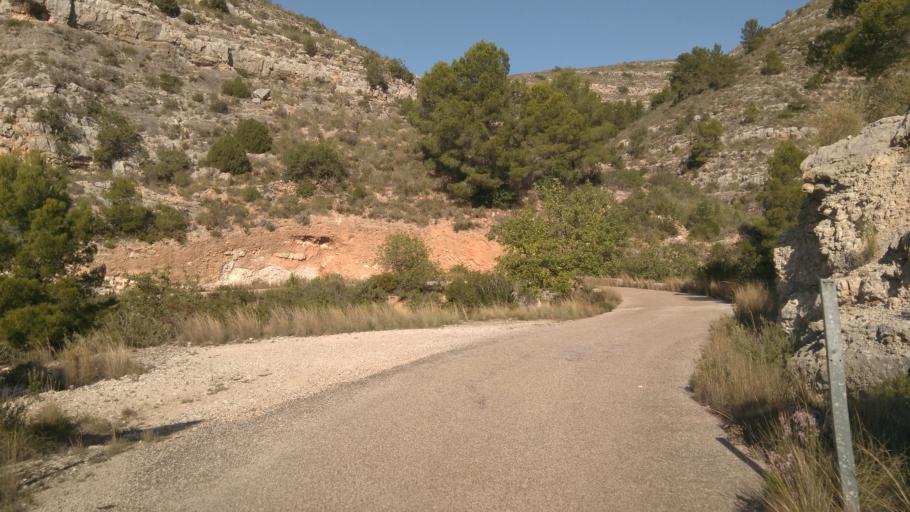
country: ES
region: Valencia
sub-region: Provincia de Valencia
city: Sumacarcer
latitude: 39.1549
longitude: -0.6511
